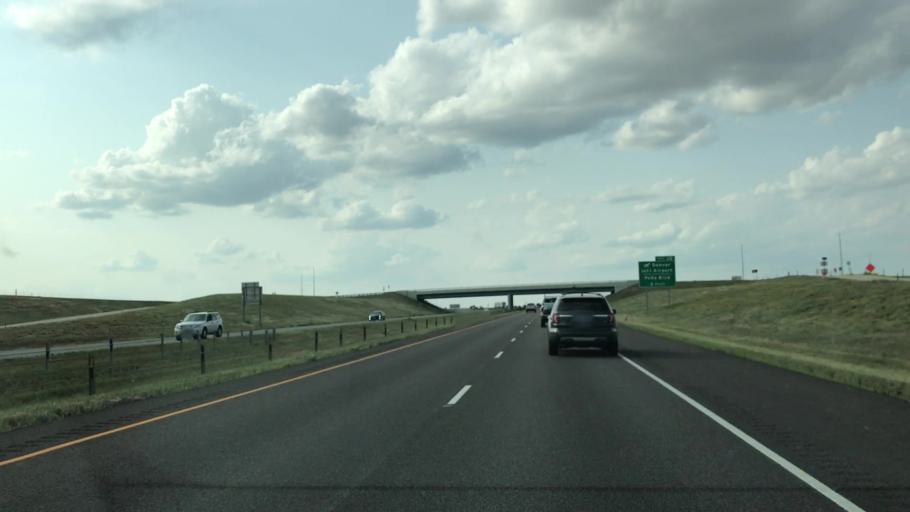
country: US
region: Colorado
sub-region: Adams County
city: Aurora
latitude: 39.8103
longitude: -104.7192
